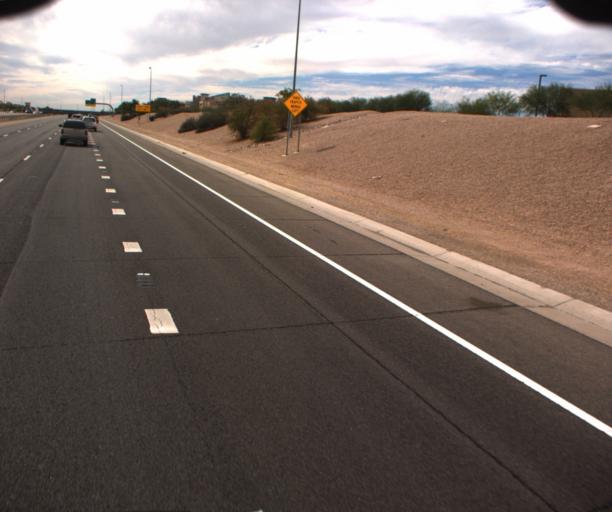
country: US
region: Arizona
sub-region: Maricopa County
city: Gilbert
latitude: 33.2932
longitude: -111.7473
